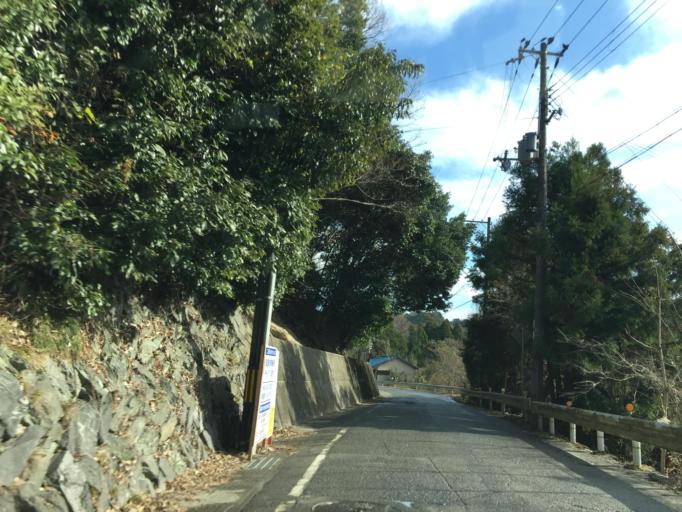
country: JP
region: Wakayama
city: Iwade
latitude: 34.1487
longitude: 135.3589
